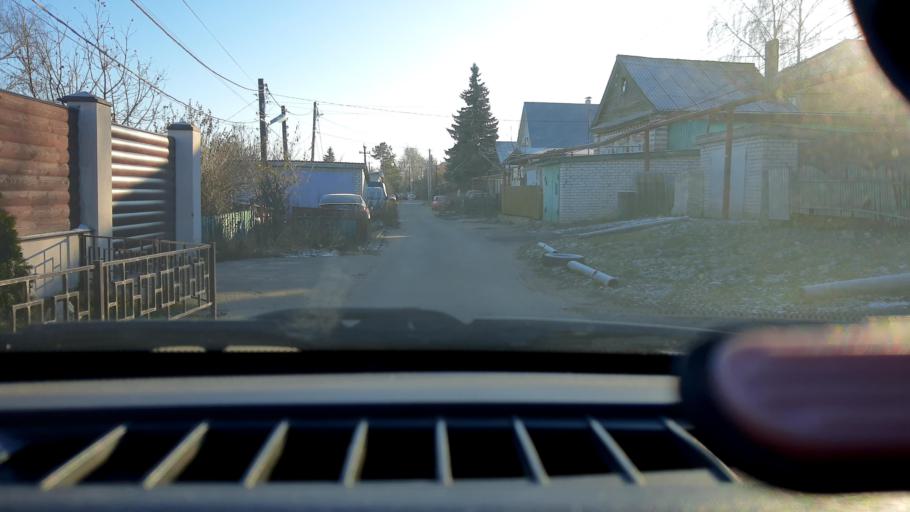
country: RU
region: Nizjnij Novgorod
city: Afonino
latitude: 56.3062
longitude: 44.0894
